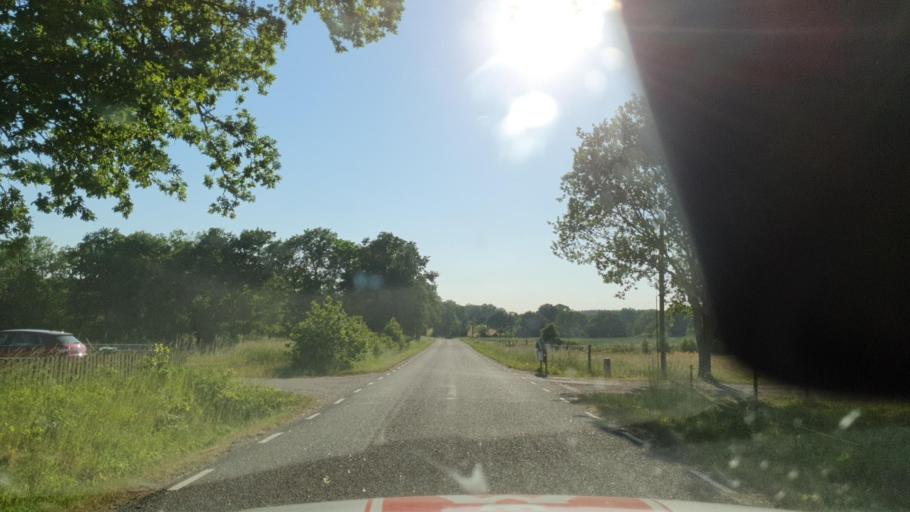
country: SE
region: Kalmar
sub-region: Kalmar Kommun
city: Ljungbyholm
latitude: 56.5008
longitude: 16.1179
